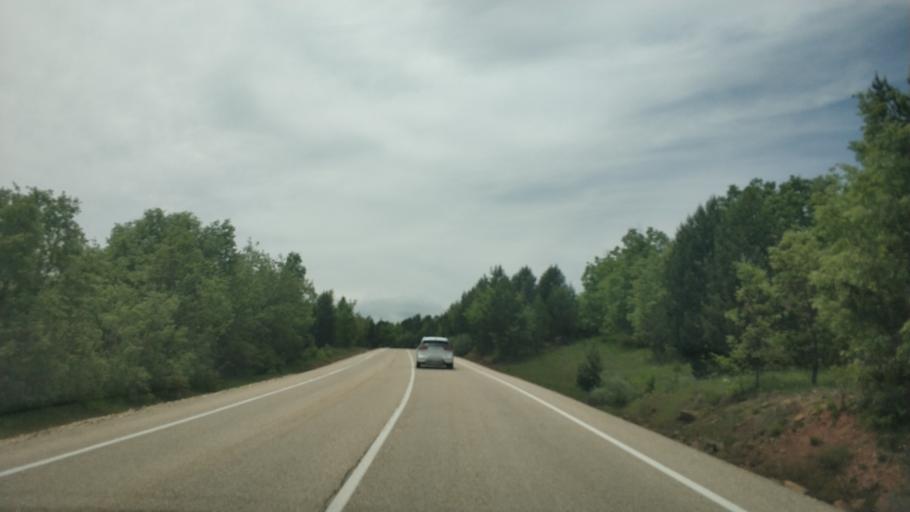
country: ES
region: Castille and Leon
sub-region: Provincia de Soria
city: Vinuesa
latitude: 41.8862
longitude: -2.7042
